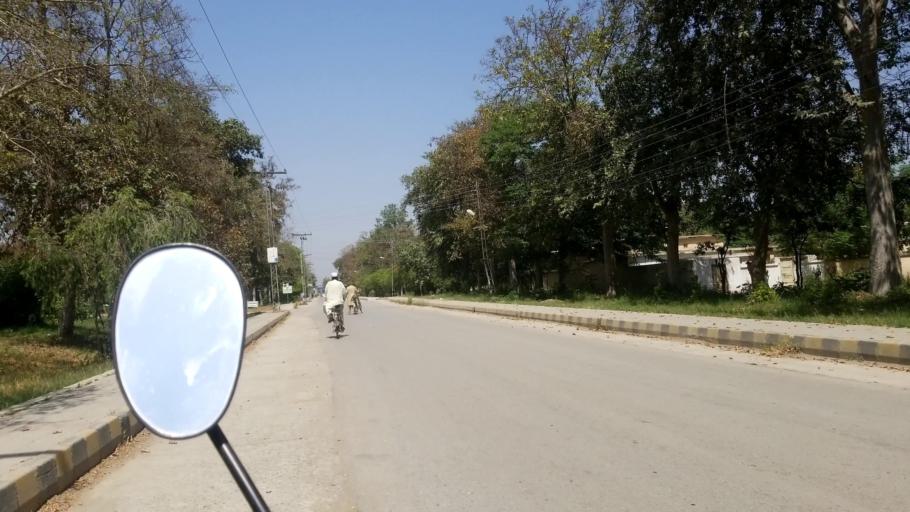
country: PK
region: Khyber Pakhtunkhwa
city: Peshawar
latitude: 34.0156
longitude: 71.4835
